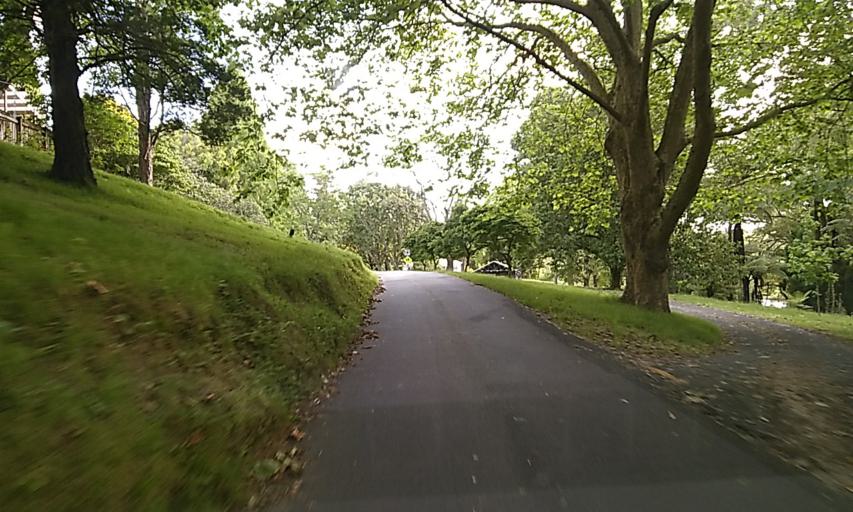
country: NZ
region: Bay of Plenty
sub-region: Tauranga City
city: Tauranga
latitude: -37.8083
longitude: 176.0460
